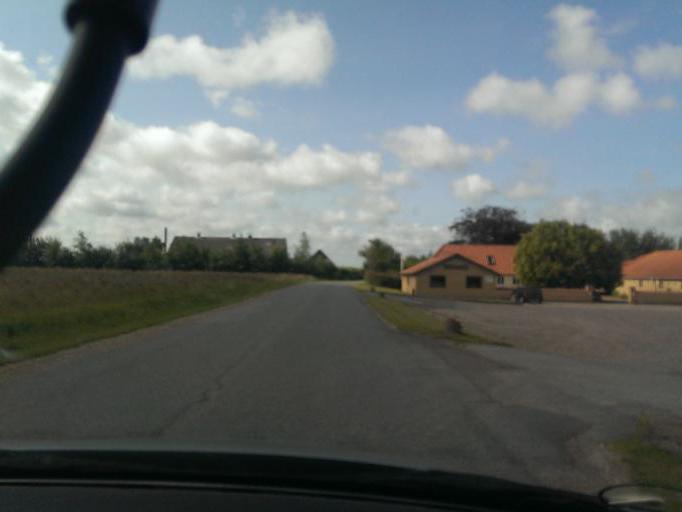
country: DK
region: North Denmark
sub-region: Hjorring Kommune
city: Vra
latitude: 57.3448
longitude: 9.9429
